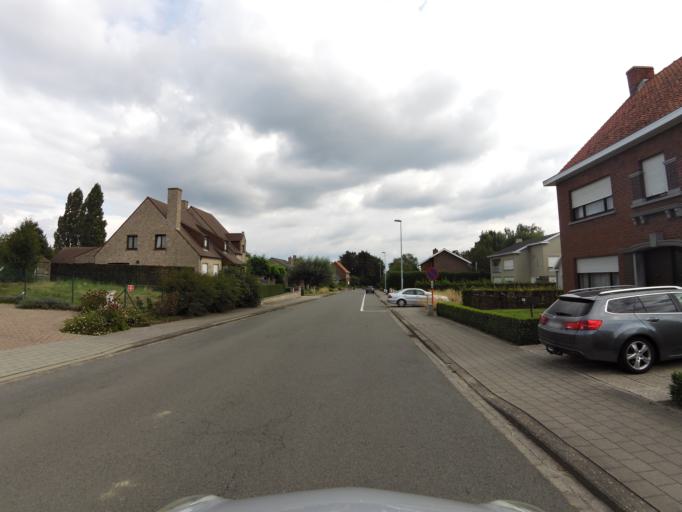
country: BE
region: Flanders
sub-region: Provincie West-Vlaanderen
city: Tielt
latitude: 50.9967
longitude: 3.3384
